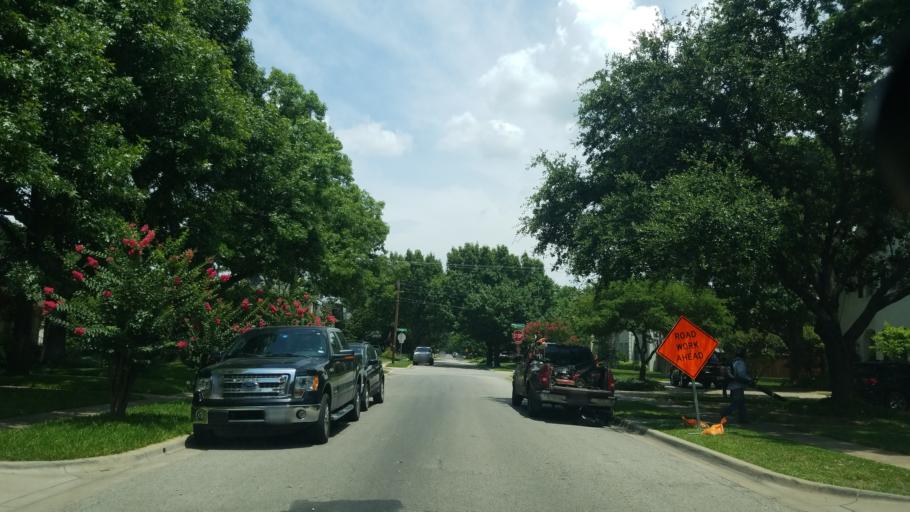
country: US
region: Texas
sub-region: Dallas County
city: University Park
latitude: 32.8540
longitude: -96.8093
